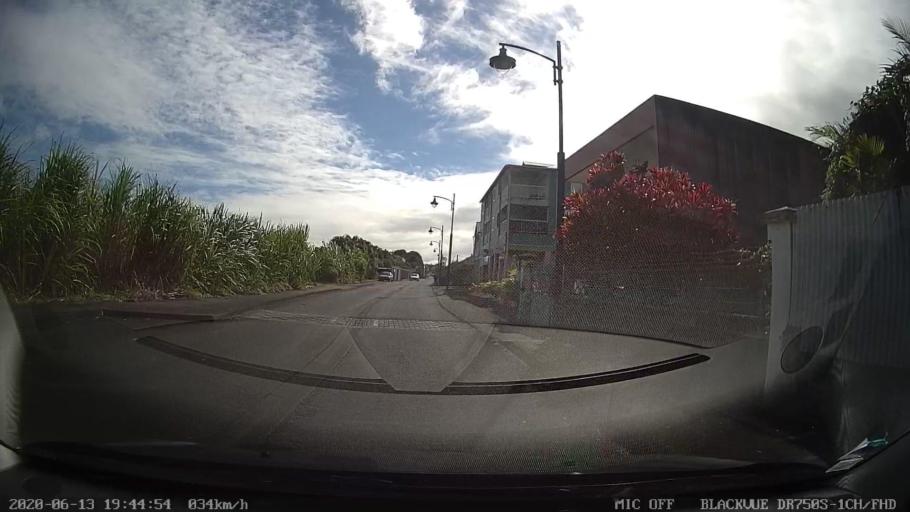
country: RE
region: Reunion
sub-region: Reunion
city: Bras-Panon
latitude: -20.9996
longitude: 55.6766
